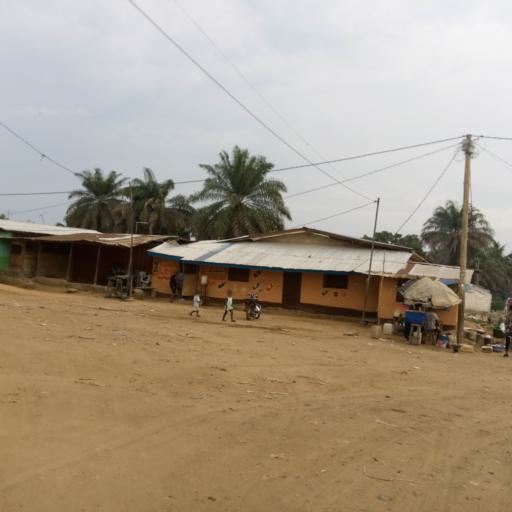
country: LR
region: Montserrado
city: Monrovia
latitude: 6.2971
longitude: -10.6870
